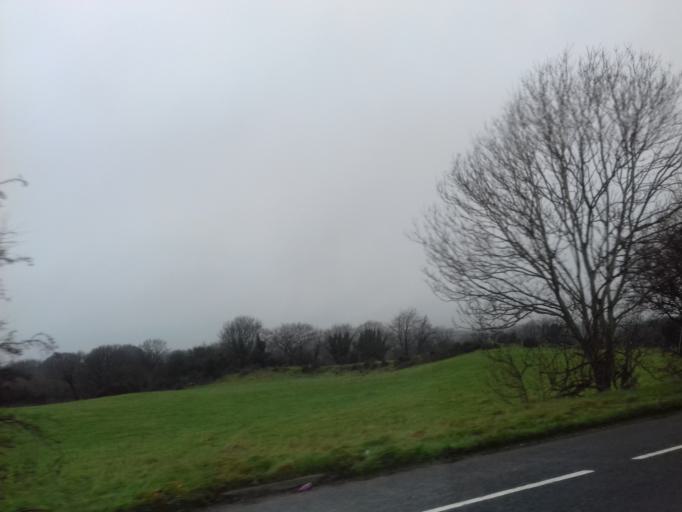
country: GB
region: Northern Ireland
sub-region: Strabane District
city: Sion Mills
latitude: 54.7457
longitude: -7.4420
